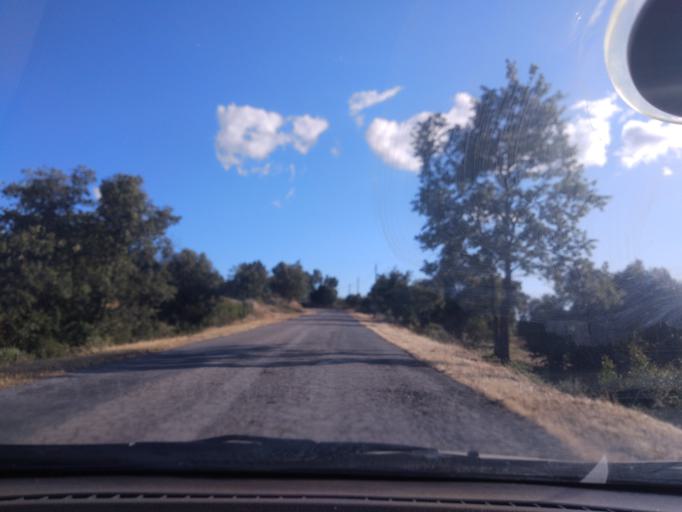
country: PT
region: Castelo Branco
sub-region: Covilha
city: Teixoso
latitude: 40.2445
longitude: -7.3843
